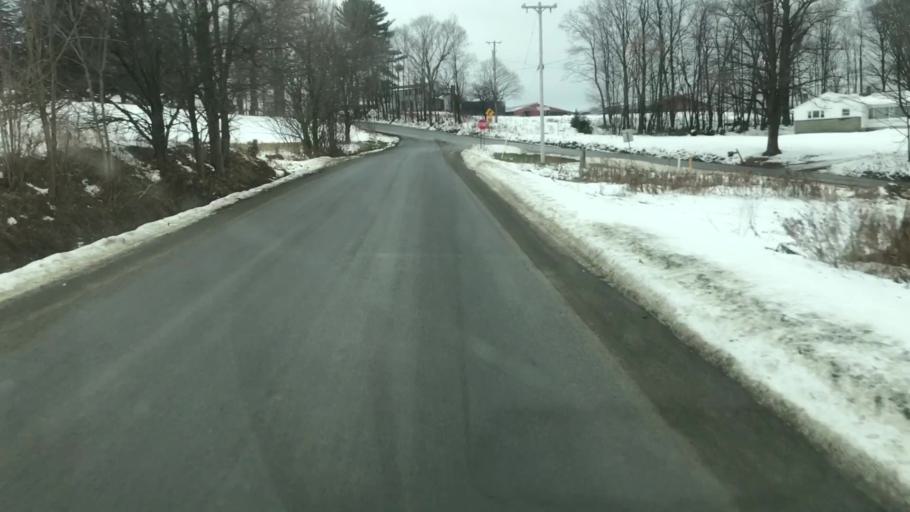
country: US
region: New York
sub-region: Cortland County
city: Cortland West
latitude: 42.6471
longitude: -76.2547
